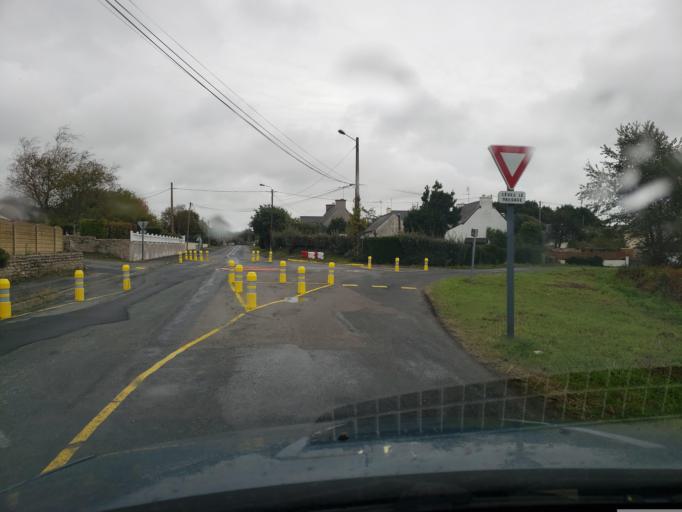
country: FR
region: Brittany
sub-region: Departement du Finistere
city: Treffiagat
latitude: 47.8065
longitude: -4.2685
